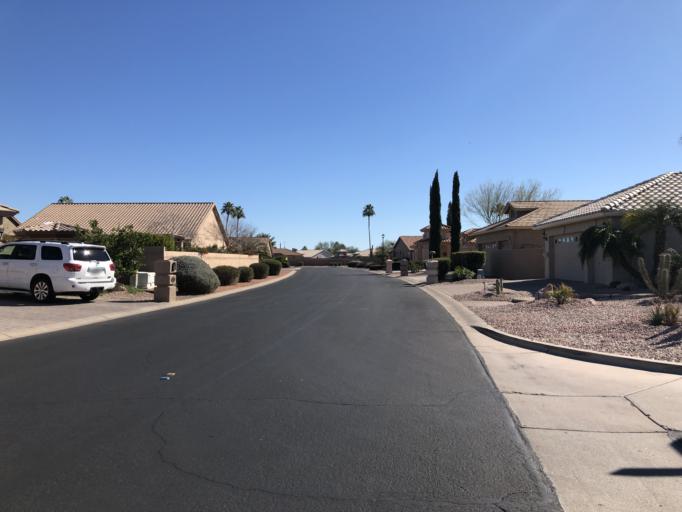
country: US
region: Arizona
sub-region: Maricopa County
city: Sun Lakes
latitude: 33.2270
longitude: -111.8851
